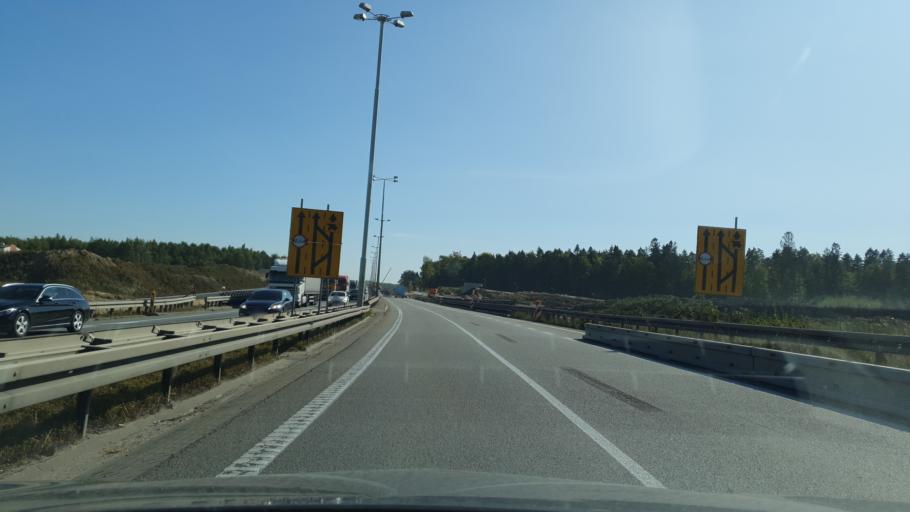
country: PL
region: Pomeranian Voivodeship
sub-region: Gdynia
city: Wielki Kack
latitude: 54.4707
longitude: 18.4734
